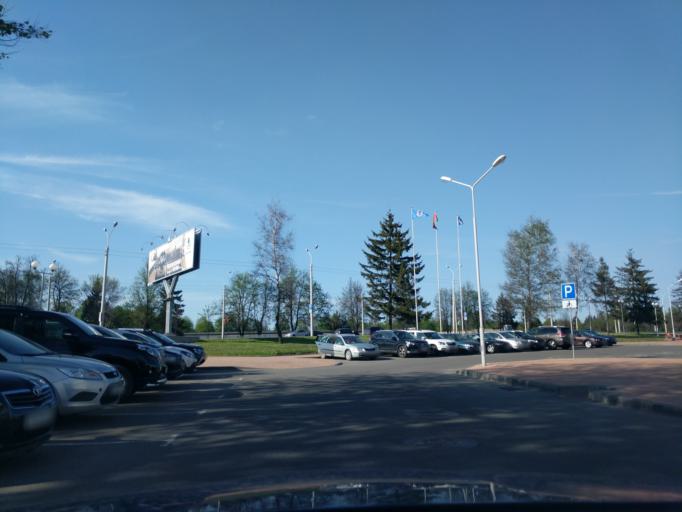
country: BY
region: Minsk
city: Lyeskawka
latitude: 53.9506
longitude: 27.7068
